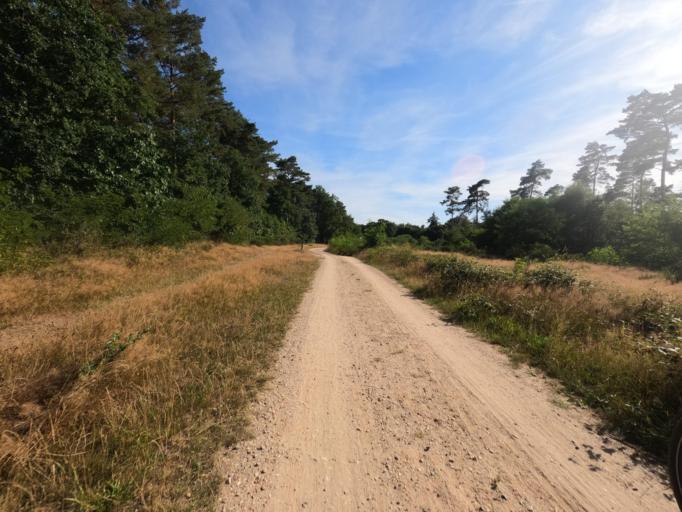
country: NL
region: Limburg
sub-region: Gemeente Beesel
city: Beesel
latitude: 51.2351
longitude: 6.0697
